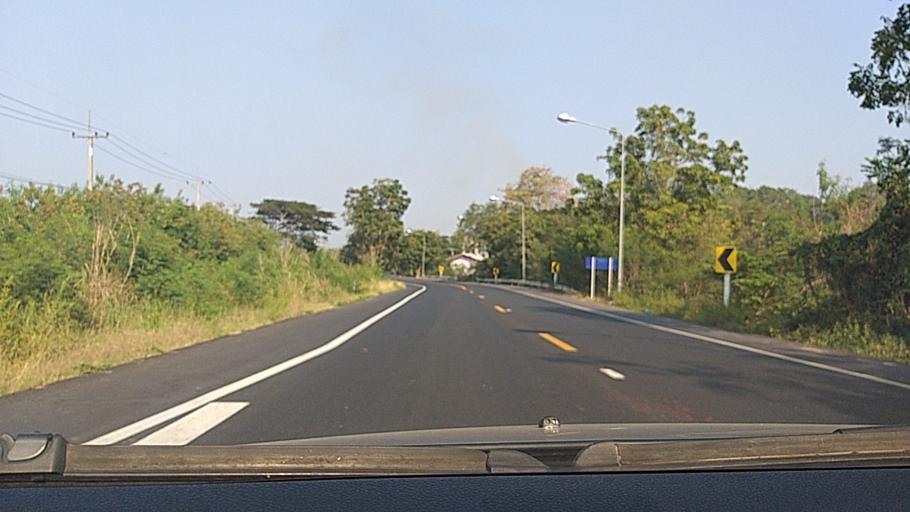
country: TH
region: Sing Buri
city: Phrom Buri
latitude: 14.7606
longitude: 100.4371
